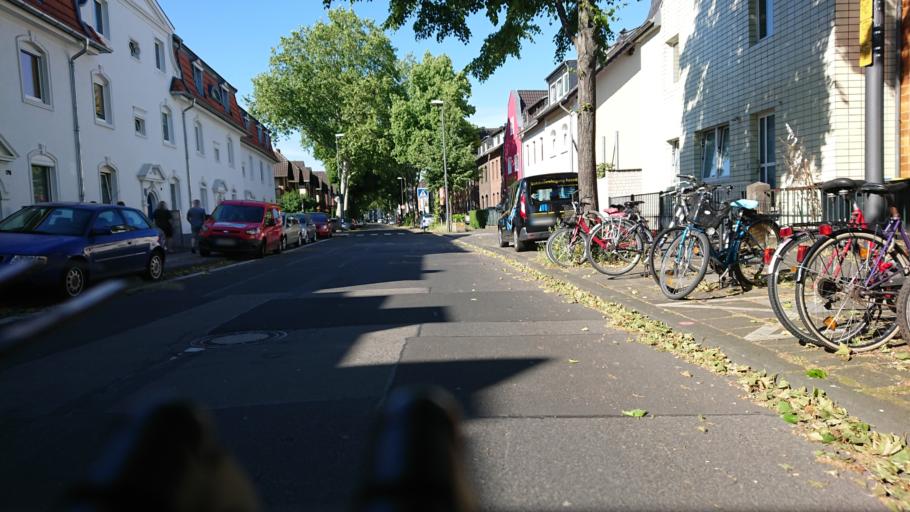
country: DE
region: North Rhine-Westphalia
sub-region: Regierungsbezirk Koln
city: Mengenich
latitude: 50.9449
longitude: 6.8842
